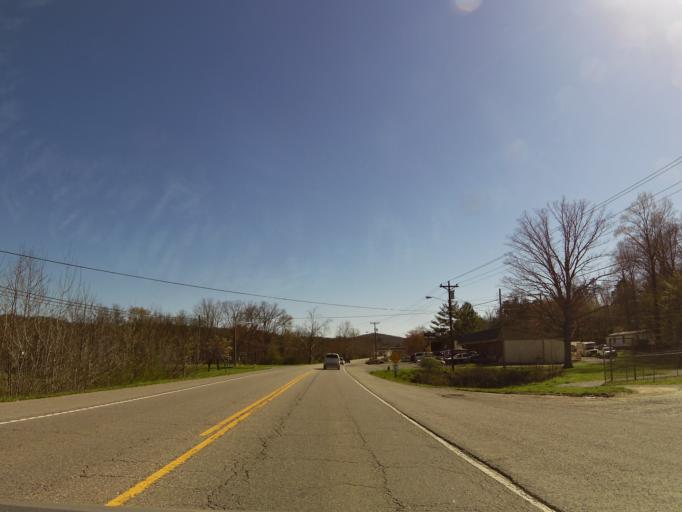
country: US
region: Tennessee
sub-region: Scott County
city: Oneida
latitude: 36.5550
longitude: -84.4511
